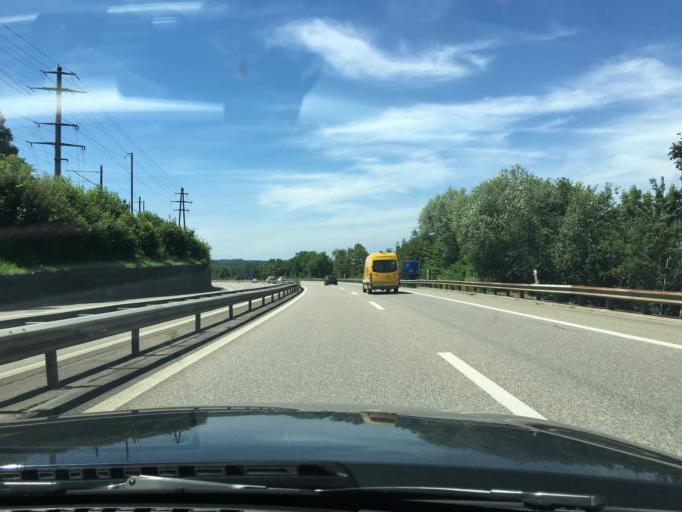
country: DE
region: Baden-Wuerttemberg
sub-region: Freiburg Region
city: Bad Sackingen
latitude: 47.5441
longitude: 7.9380
